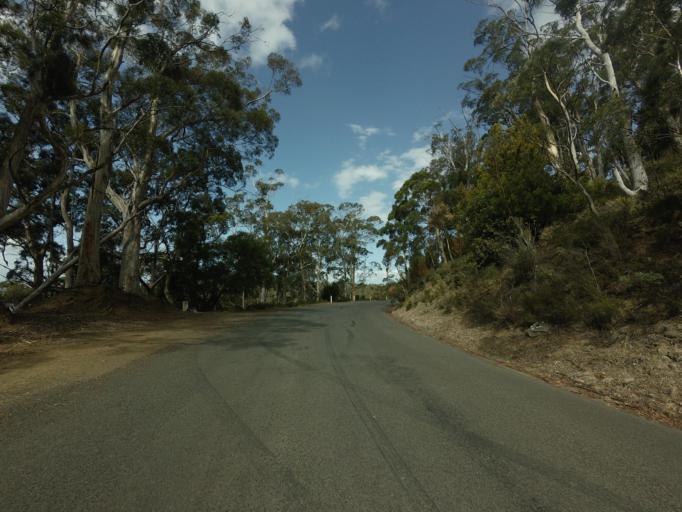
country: AU
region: Tasmania
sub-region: Hobart
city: Dynnyrne
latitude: -42.9153
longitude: 147.2817
